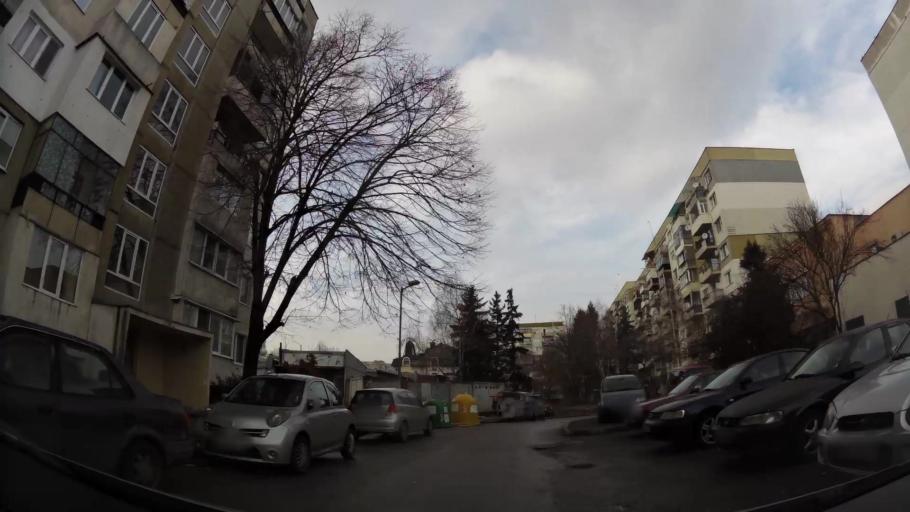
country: BG
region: Sofiya
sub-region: Obshtina Bozhurishte
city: Bozhurishte
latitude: 42.7182
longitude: 23.2481
